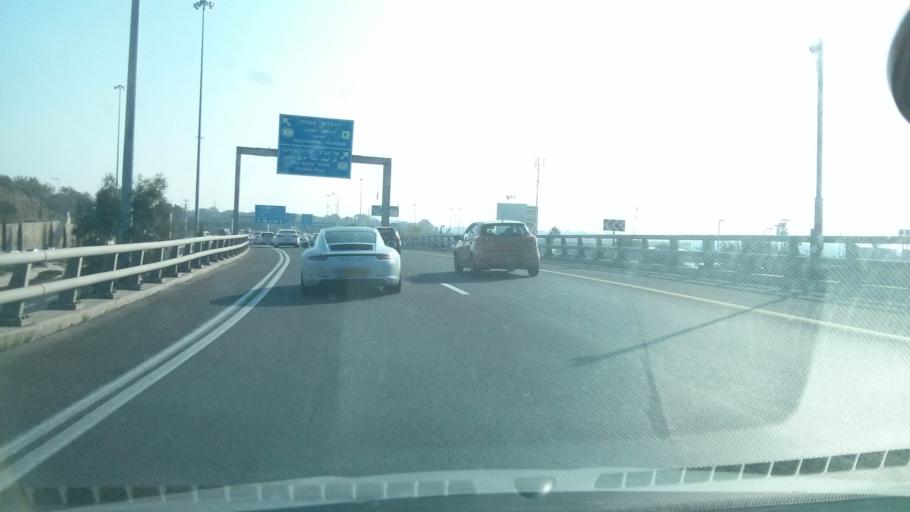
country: IL
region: Tel Aviv
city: Herzliya Pituah
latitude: 32.1401
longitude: 34.8023
